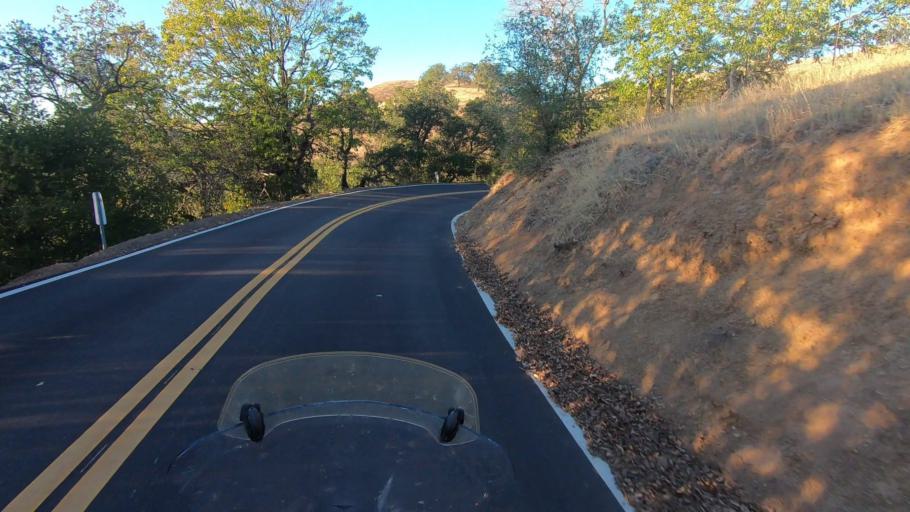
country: US
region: California
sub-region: Santa Clara County
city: East Foothills
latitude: 37.3293
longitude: -121.6843
